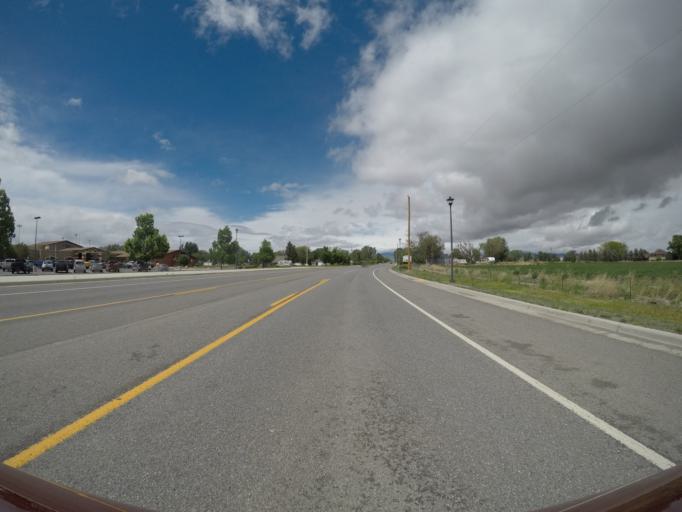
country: US
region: Wyoming
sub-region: Big Horn County
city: Lovell
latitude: 44.8757
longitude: -108.4627
